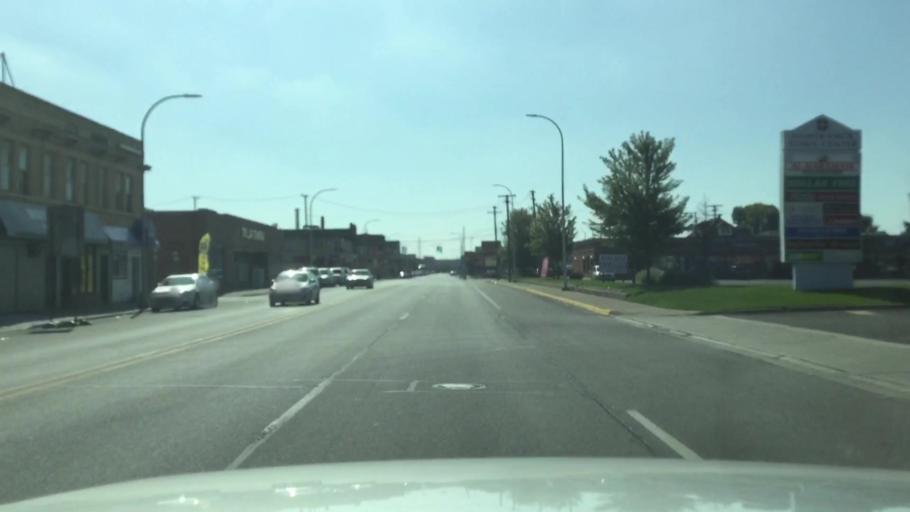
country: US
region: Michigan
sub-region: Wayne County
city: Hamtramck
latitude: 42.3928
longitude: -83.0552
